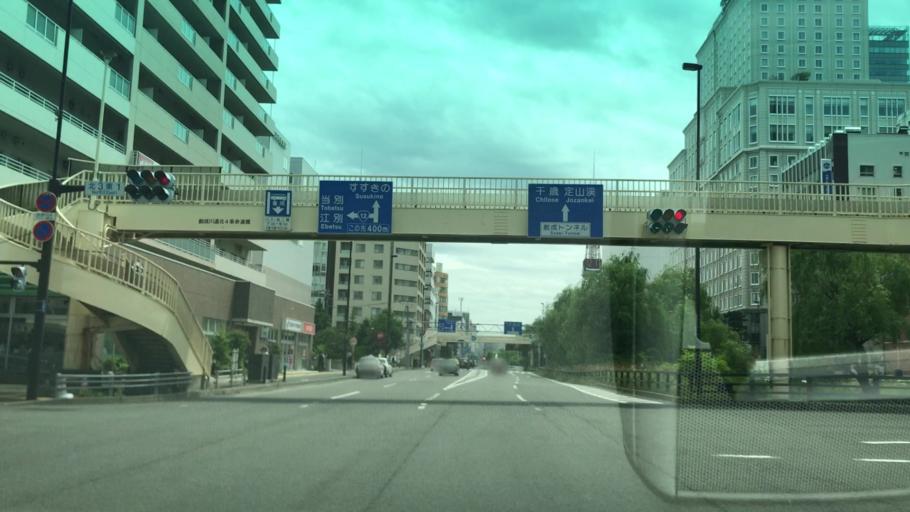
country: JP
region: Hokkaido
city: Sapporo
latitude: 43.0664
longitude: 141.3559
